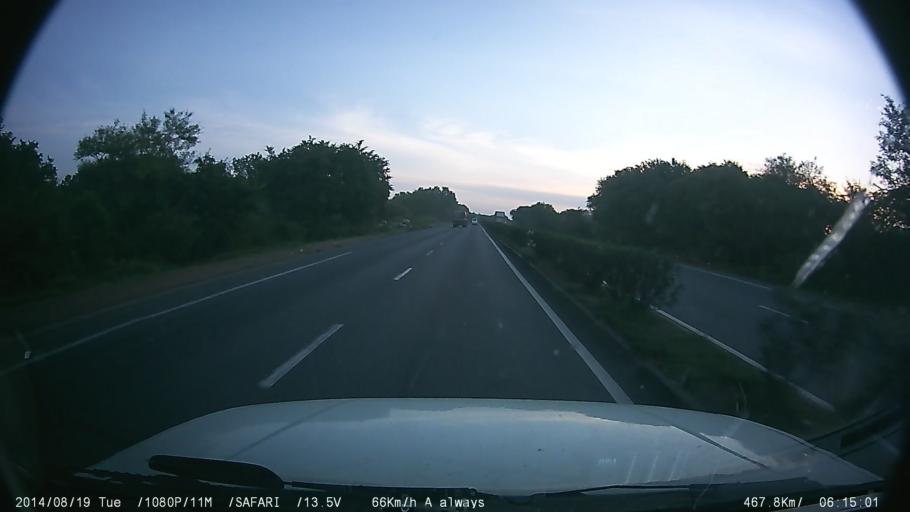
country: IN
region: Tamil Nadu
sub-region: Dharmapuri
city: Dharmapuri
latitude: 11.9783
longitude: 78.0552
